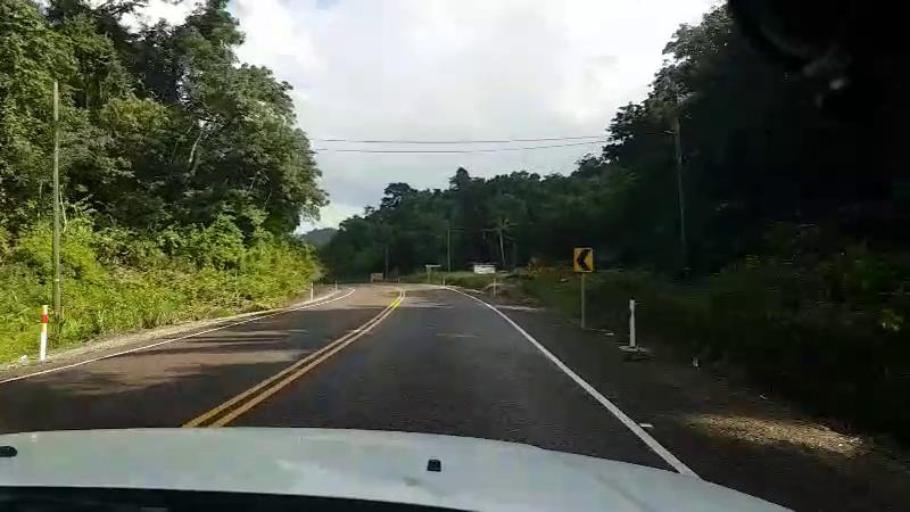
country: BZ
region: Cayo
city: Belmopan
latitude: 17.1495
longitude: -88.7141
